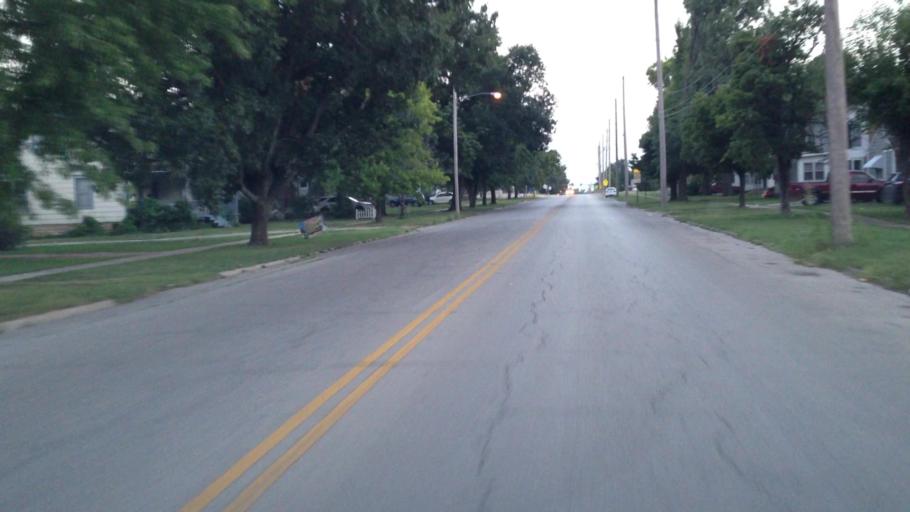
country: US
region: Kansas
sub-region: Montgomery County
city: Independence
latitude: 37.2308
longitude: -95.7108
